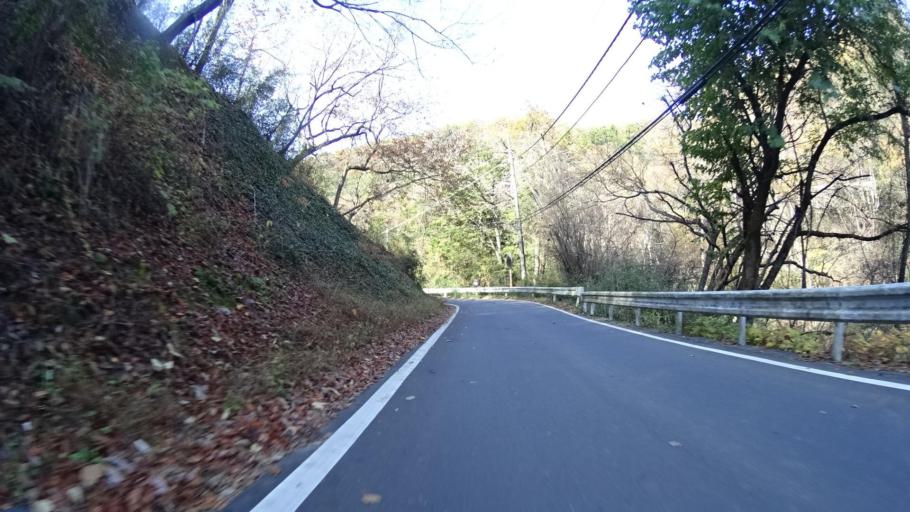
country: JP
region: Yamanashi
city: Uenohara
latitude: 35.5859
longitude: 139.1616
